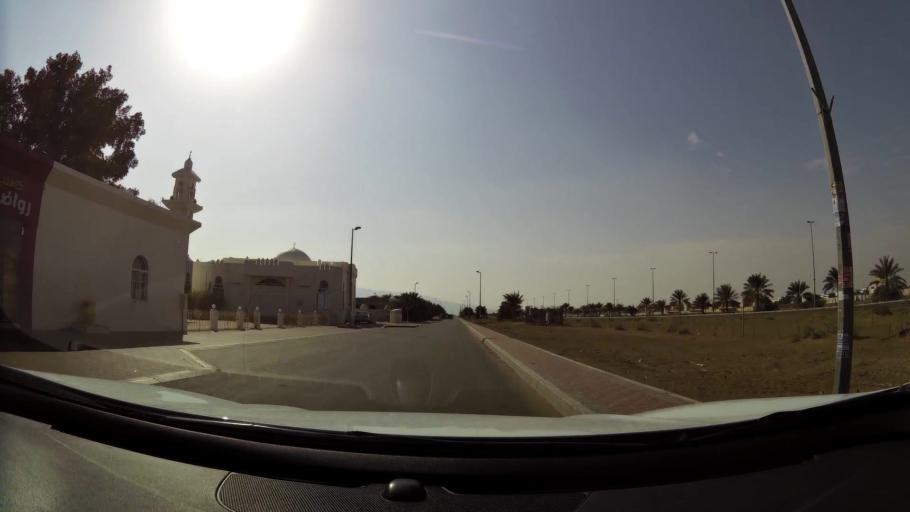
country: AE
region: Abu Dhabi
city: Al Ain
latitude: 24.0927
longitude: 55.9031
